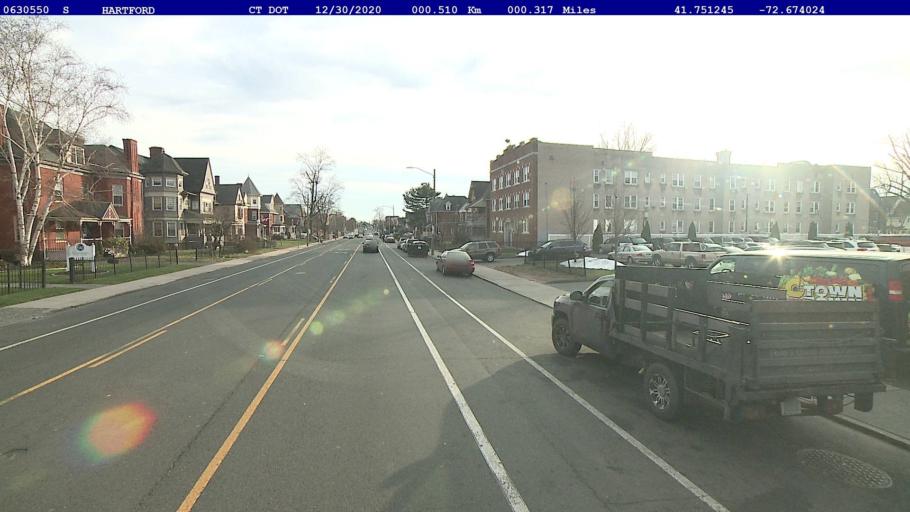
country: US
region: Connecticut
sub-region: Hartford County
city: Hartford
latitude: 41.7512
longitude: -72.6740
